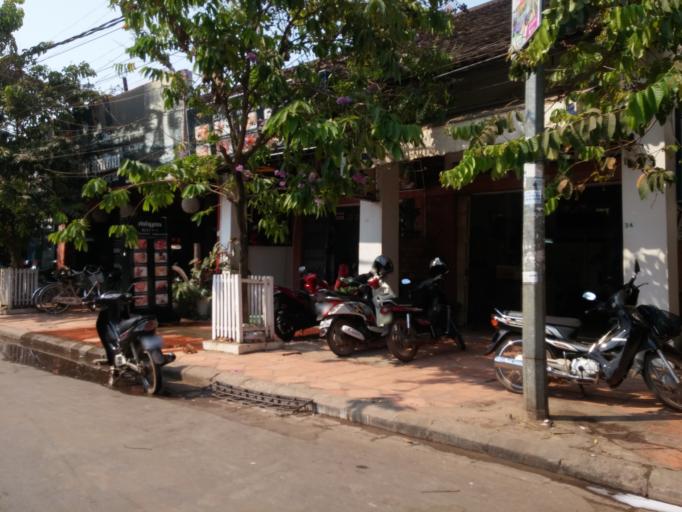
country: KH
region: Siem Reap
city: Siem Reap
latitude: 13.3562
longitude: 103.8545
